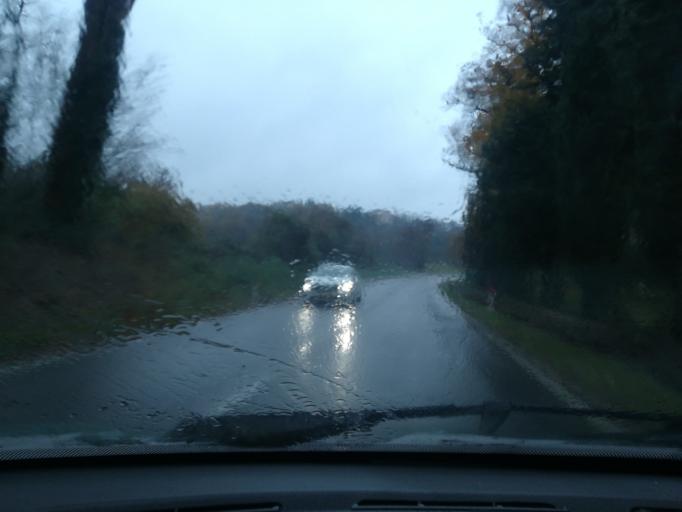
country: IT
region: The Marches
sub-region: Provincia di Macerata
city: Sforzacosta
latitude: 43.2721
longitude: 13.4267
